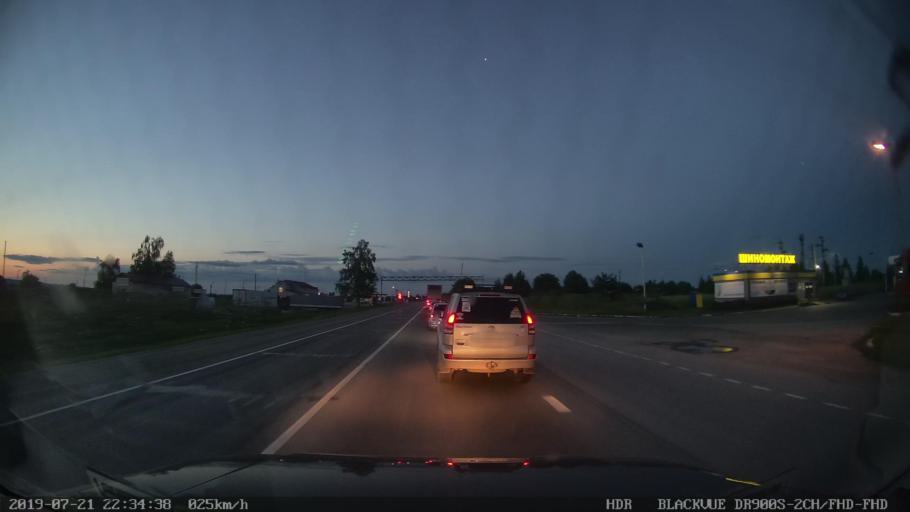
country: RU
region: Perm
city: Chaykovskaya
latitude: 58.0411
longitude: 55.5752
